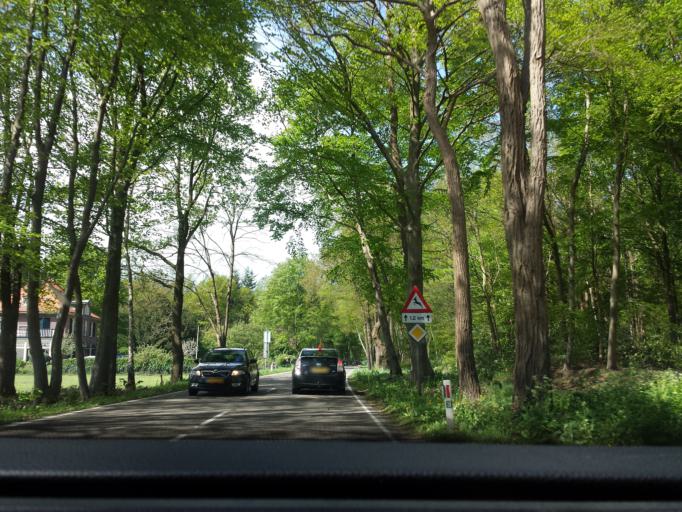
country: NL
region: Gelderland
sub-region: Gemeente Lochem
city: Barchem
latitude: 52.0969
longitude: 6.4500
